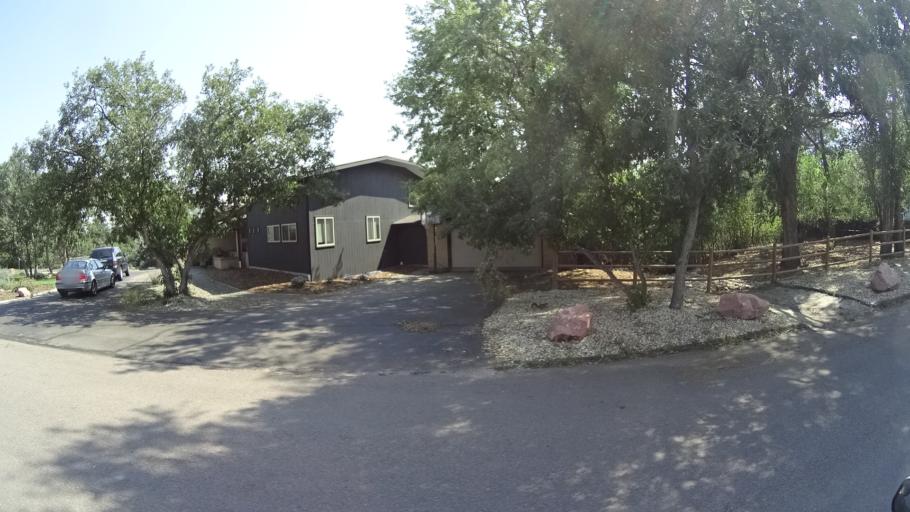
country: US
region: Colorado
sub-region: El Paso County
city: Colorado Springs
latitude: 38.7979
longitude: -104.8297
